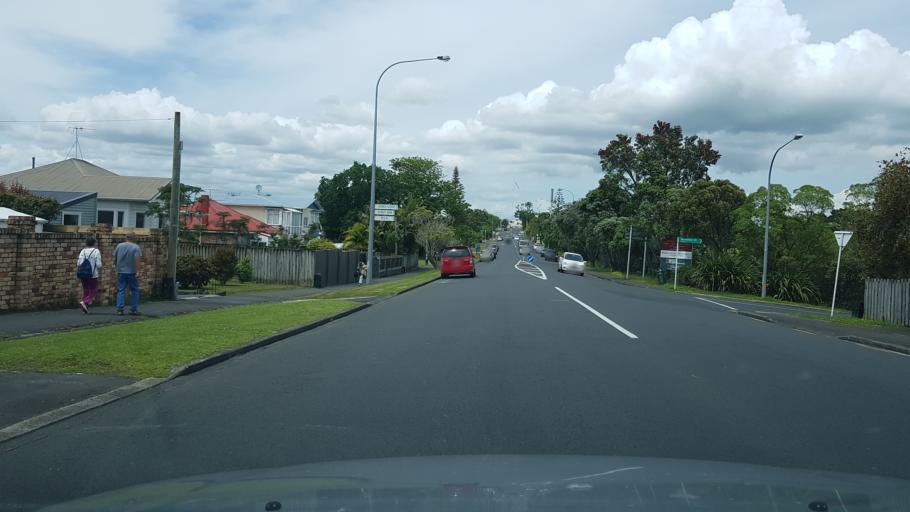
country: NZ
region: Auckland
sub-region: Auckland
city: North Shore
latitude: -36.8051
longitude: 174.7254
